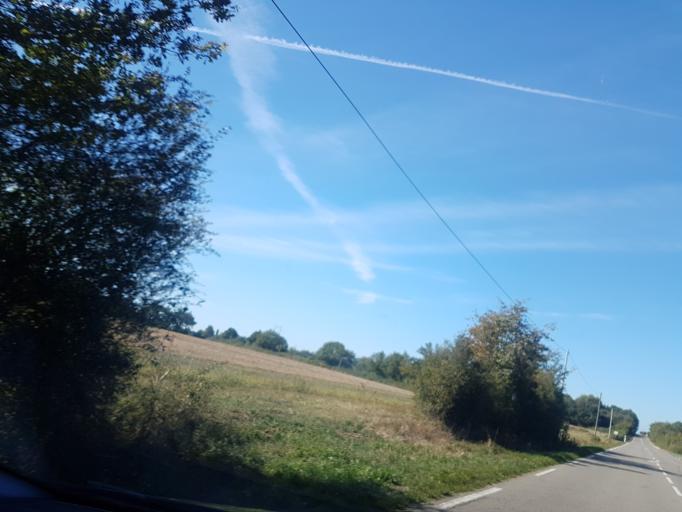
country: FR
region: Pays de la Loire
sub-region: Departement de la Loire-Atlantique
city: Casson
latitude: 47.4285
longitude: -1.5657
